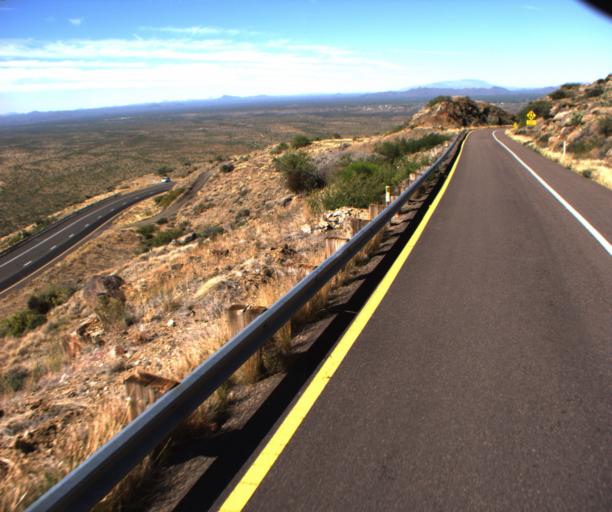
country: US
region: Arizona
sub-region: Yavapai County
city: Congress
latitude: 34.2055
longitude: -112.7863
